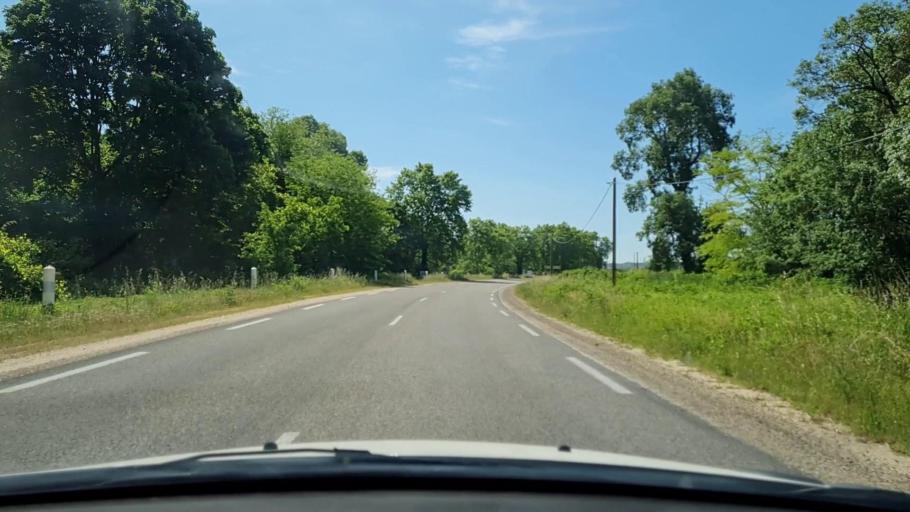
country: FR
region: Languedoc-Roussillon
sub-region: Departement du Gard
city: Saint-Genies-de-Malgoires
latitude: 43.9541
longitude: 4.2453
